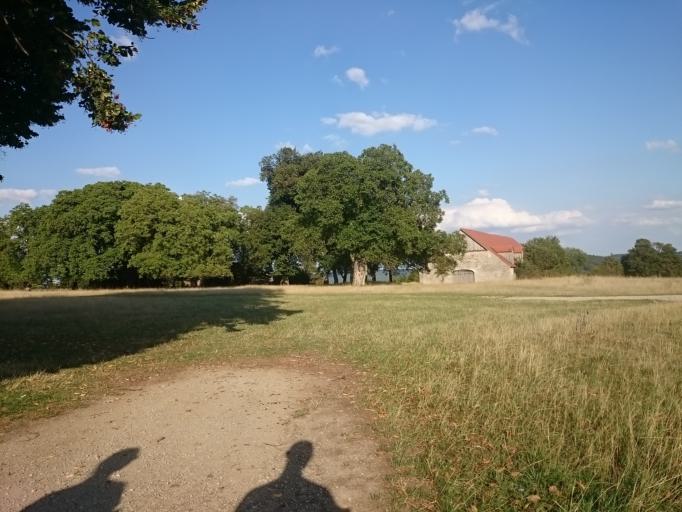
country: DE
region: Bavaria
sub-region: Regierungsbezirk Mittelfranken
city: Thalmassing
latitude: 49.1179
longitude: 11.2977
